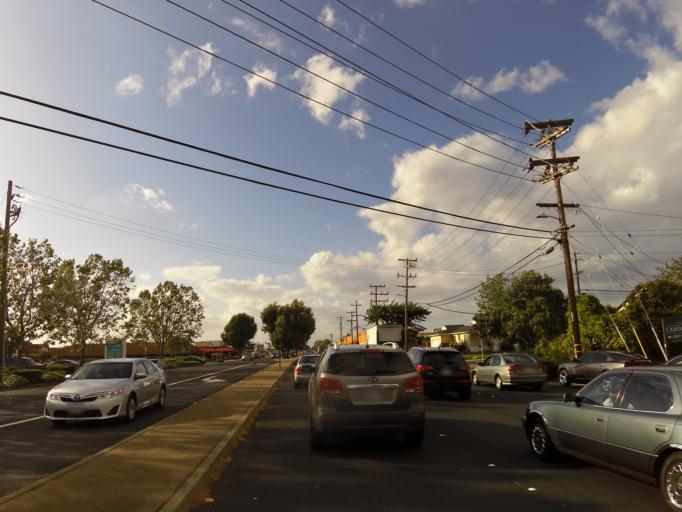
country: US
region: California
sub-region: Alameda County
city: Cherryland
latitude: 37.6508
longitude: -122.1089
